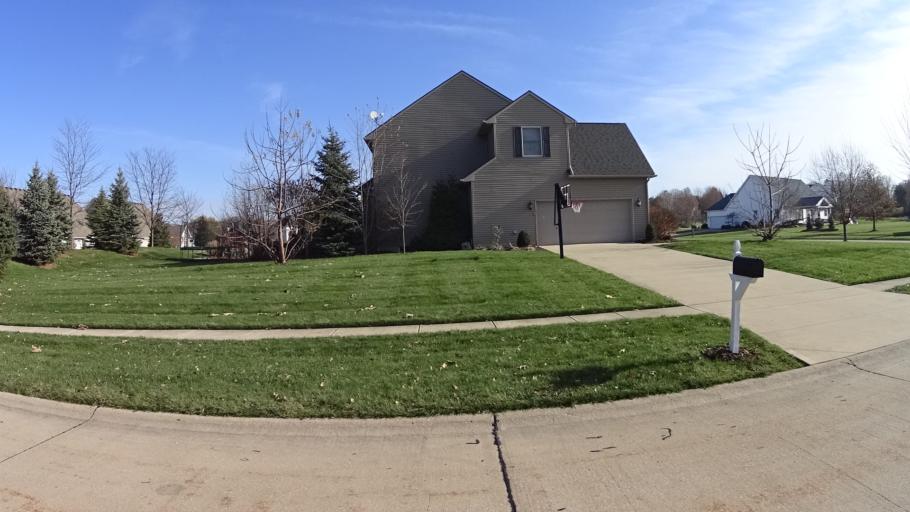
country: US
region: Ohio
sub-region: Lorain County
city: Avon
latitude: 41.4458
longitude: -82.0473
